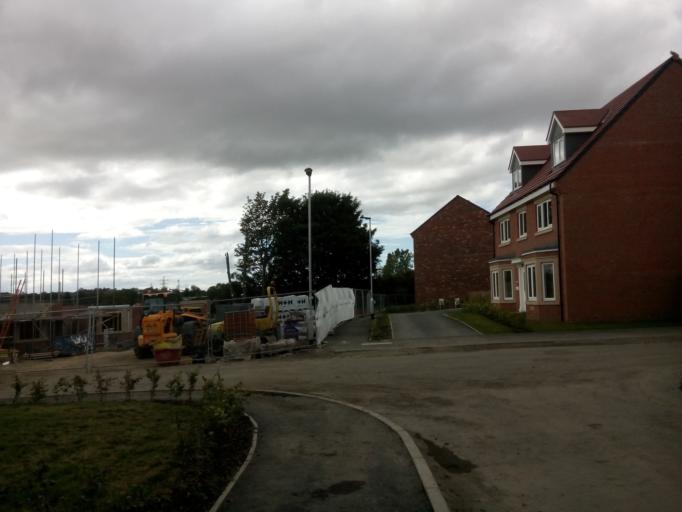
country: GB
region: England
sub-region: County Durham
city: Durham
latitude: 54.7996
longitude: -1.5819
